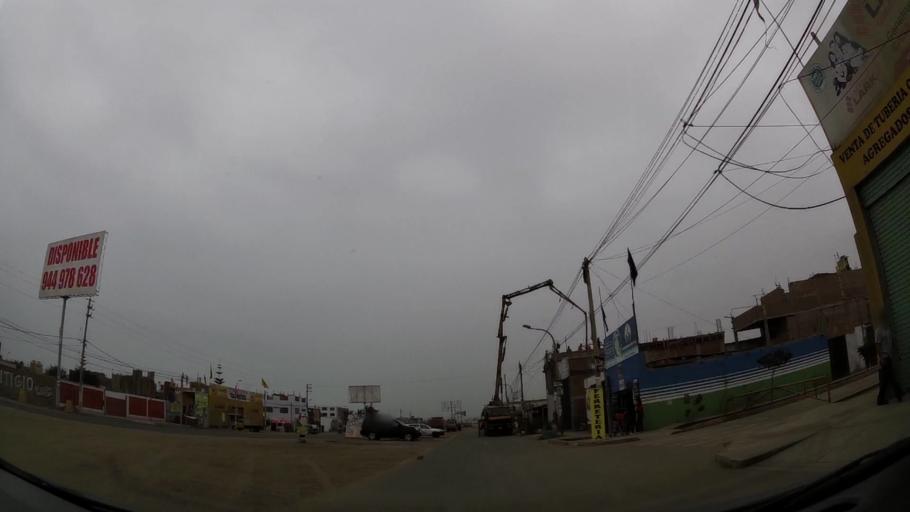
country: PE
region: Lima
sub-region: Lima
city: Punta Hermosa
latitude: -12.3087
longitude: -76.8379
